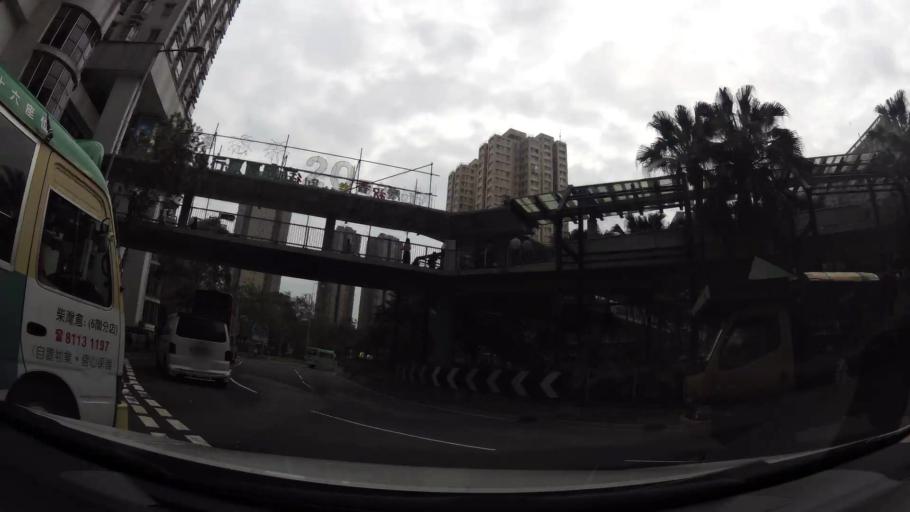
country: HK
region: Wanchai
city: Wan Chai
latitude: 22.2636
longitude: 114.2370
